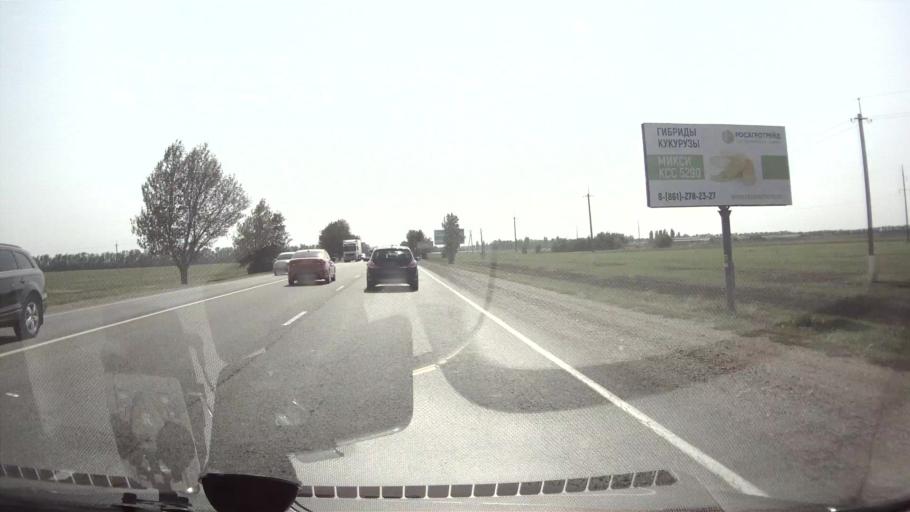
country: RU
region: Krasnodarskiy
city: Vasyurinskaya
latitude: 45.1070
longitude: 39.3879
